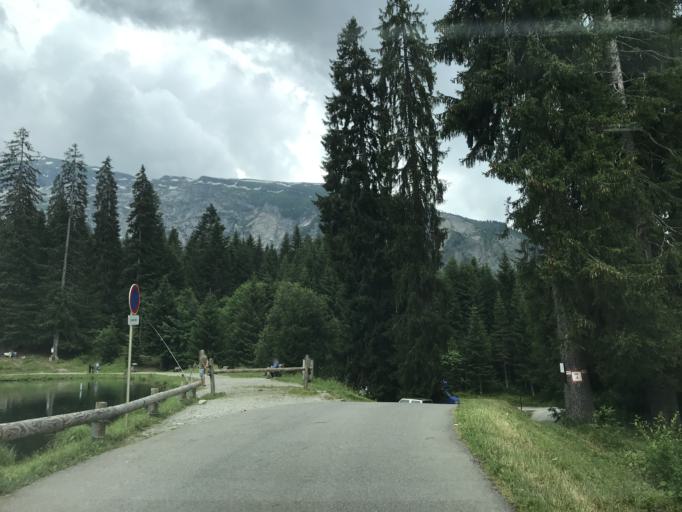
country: FR
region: Rhone-Alpes
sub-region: Departement de la Haute-Savoie
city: Morzine
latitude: 46.1490
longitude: 6.7655
